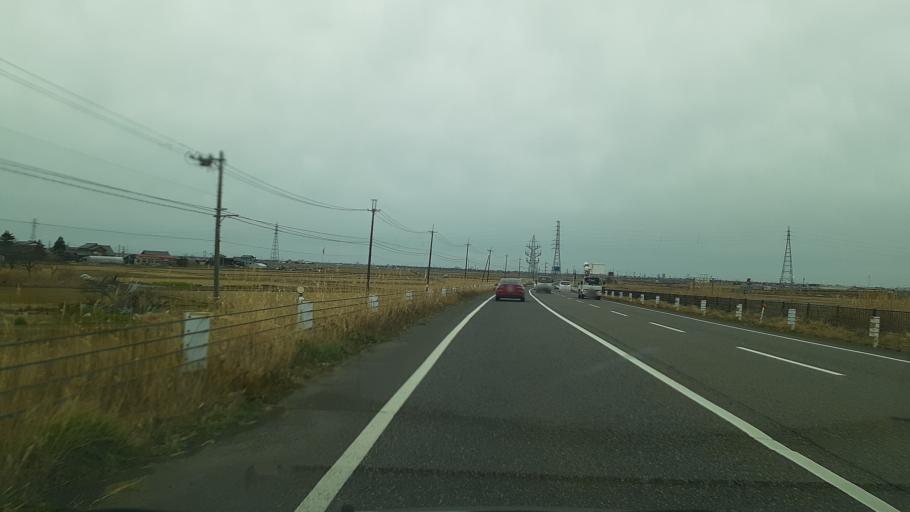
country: JP
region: Niigata
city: Niitsu-honcho
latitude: 37.7993
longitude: 139.1047
